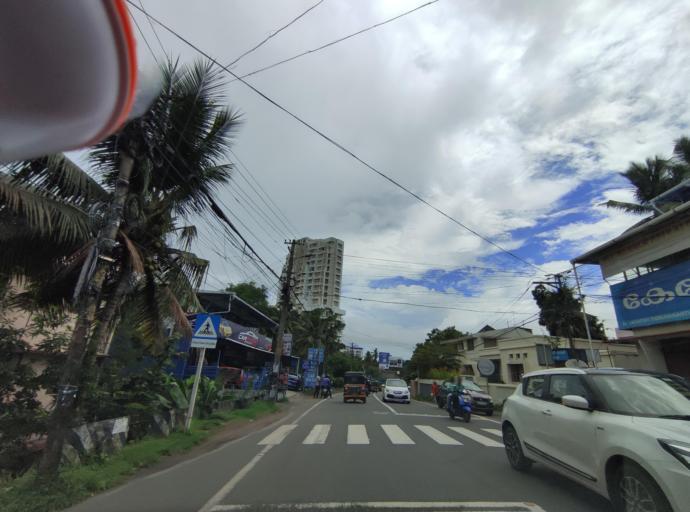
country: IN
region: Kerala
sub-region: Thiruvananthapuram
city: Thiruvananthapuram
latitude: 8.4936
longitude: 76.9672
